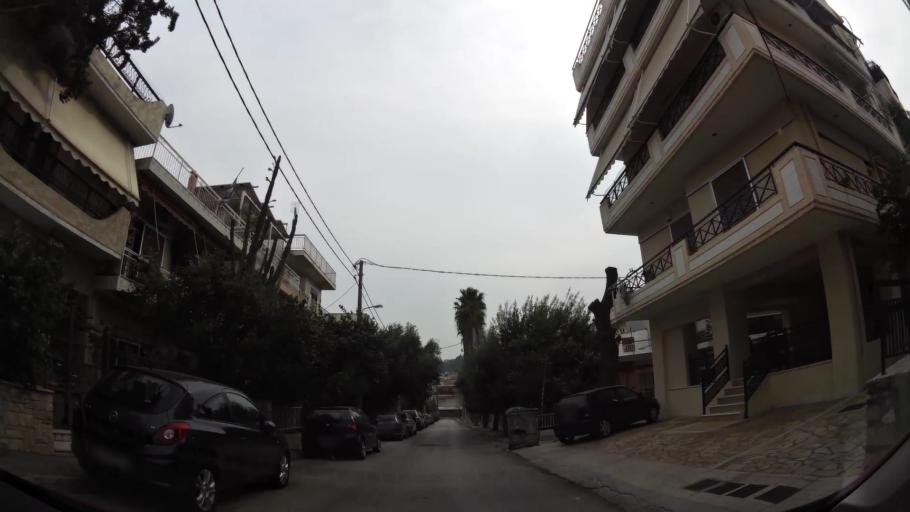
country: GR
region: Attica
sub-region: Nomarchia Athinas
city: Chaidari
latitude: 38.0144
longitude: 23.6541
